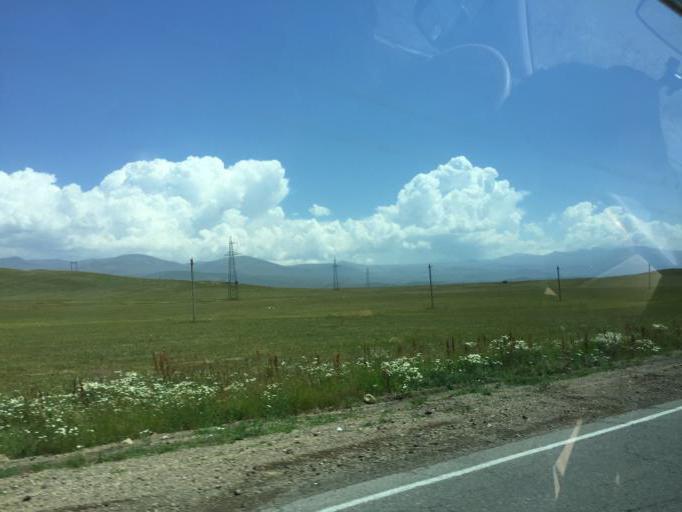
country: AM
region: Vayots' Dzori Marz
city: Jermuk
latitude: 39.6777
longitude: 45.7333
